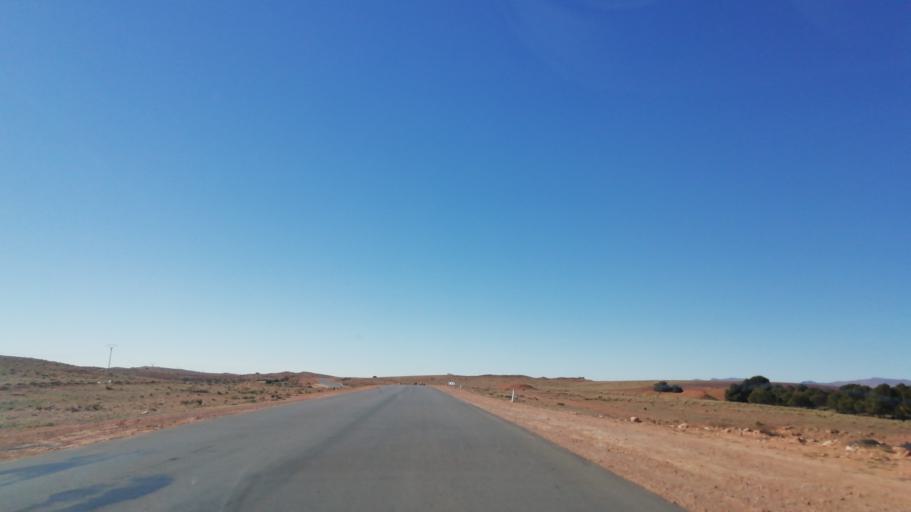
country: DZ
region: El Bayadh
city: El Bayadh
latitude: 33.6450
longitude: 1.3947
